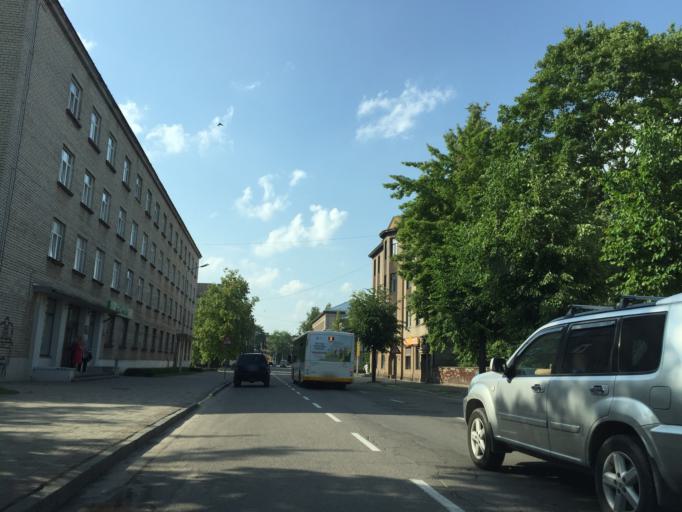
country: LV
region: Jelgava
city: Jelgava
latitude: 56.6504
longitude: 23.7293
